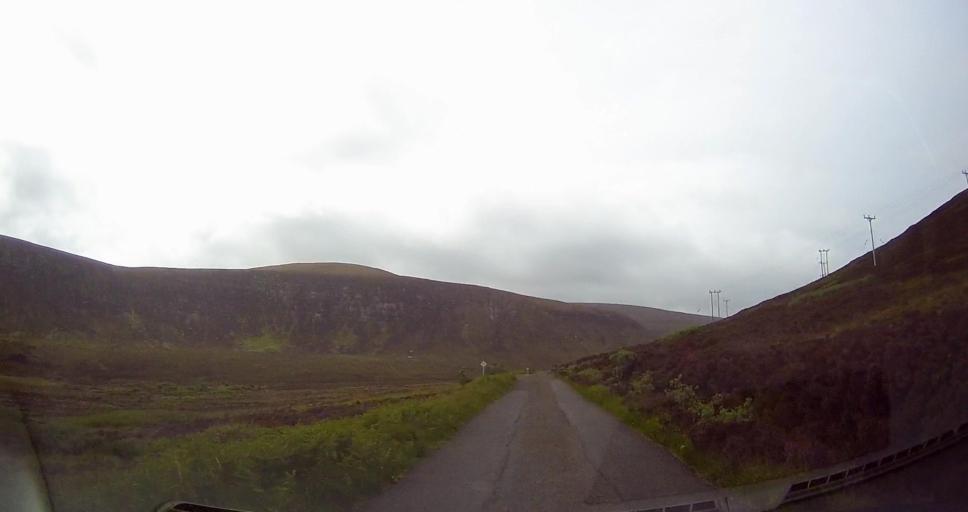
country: GB
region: Scotland
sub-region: Orkney Islands
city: Stromness
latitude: 58.8922
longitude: -3.3146
